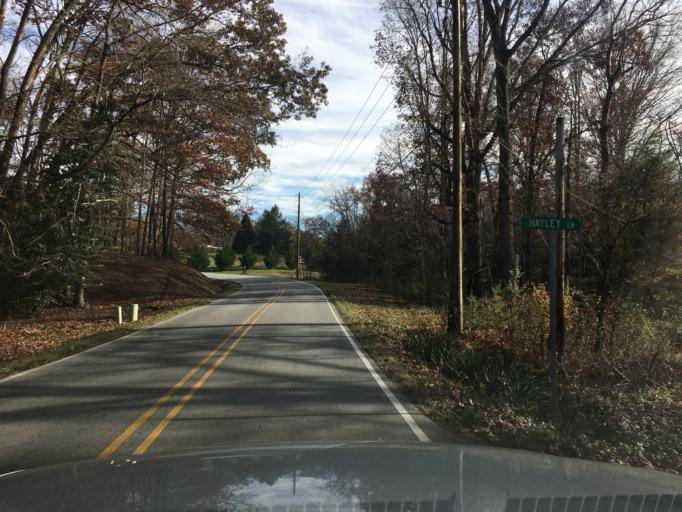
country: US
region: North Carolina
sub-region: Henderson County
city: Etowah
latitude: 35.3210
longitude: -82.6149
